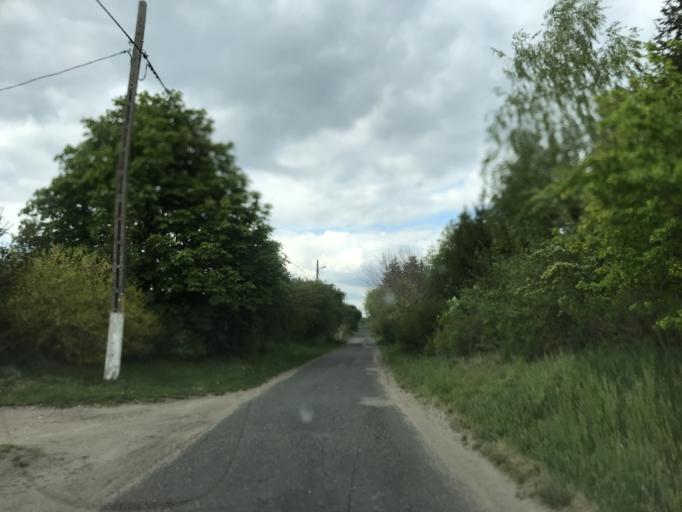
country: PL
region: West Pomeranian Voivodeship
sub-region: Powiat mysliborski
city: Mysliborz
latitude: 52.8870
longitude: 14.8970
